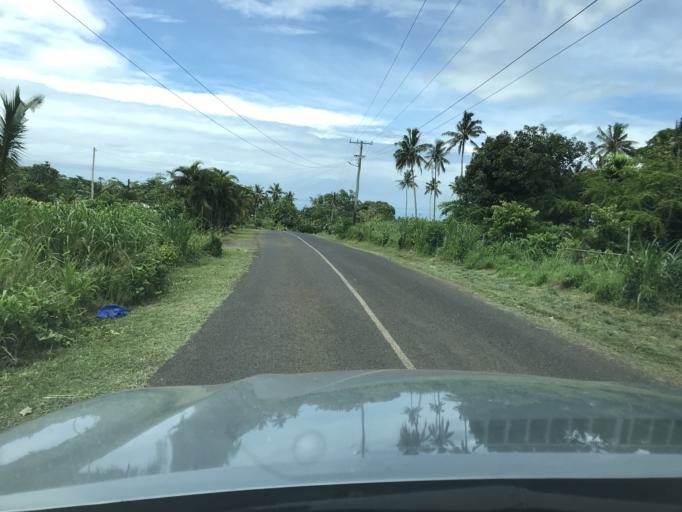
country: WS
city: Fasito`outa
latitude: -13.8675
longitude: -171.9124
